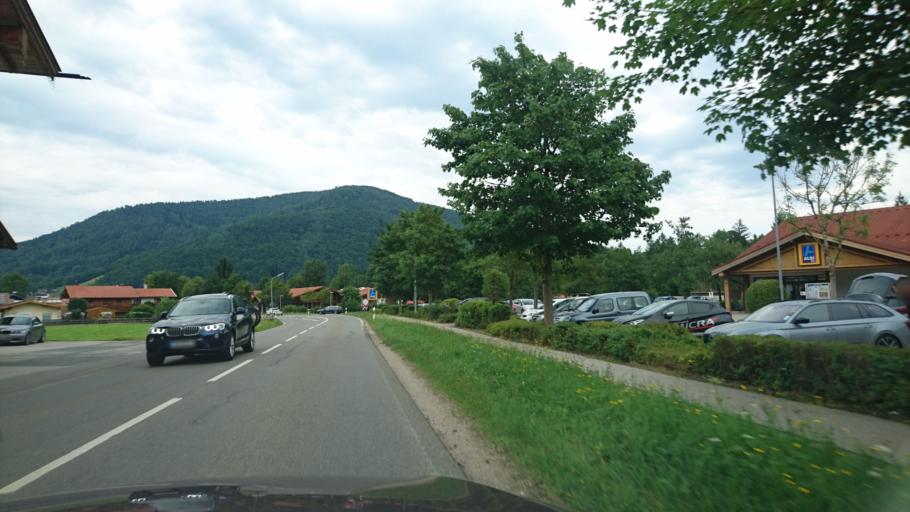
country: DE
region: Bavaria
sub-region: Upper Bavaria
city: Ruhpolding
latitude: 47.7495
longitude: 12.6554
